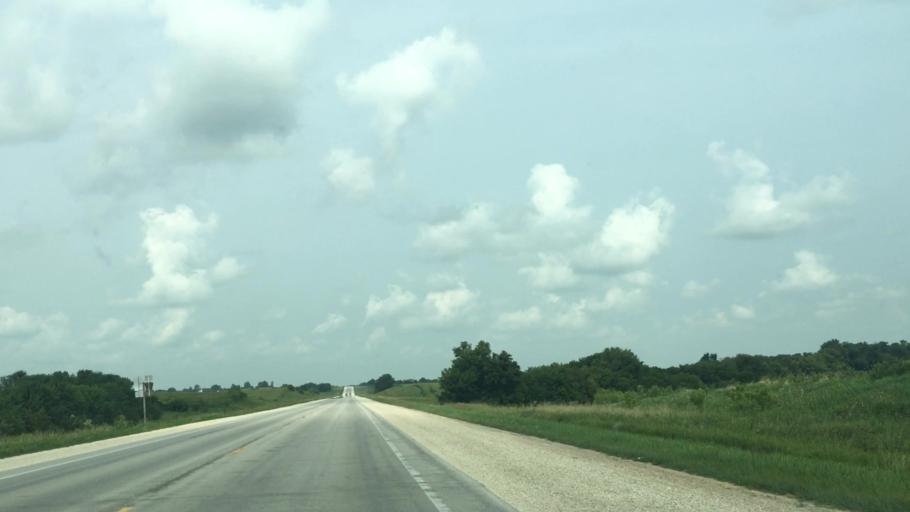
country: US
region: Iowa
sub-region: Winneshiek County
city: Decorah
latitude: 43.3698
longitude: -91.8087
